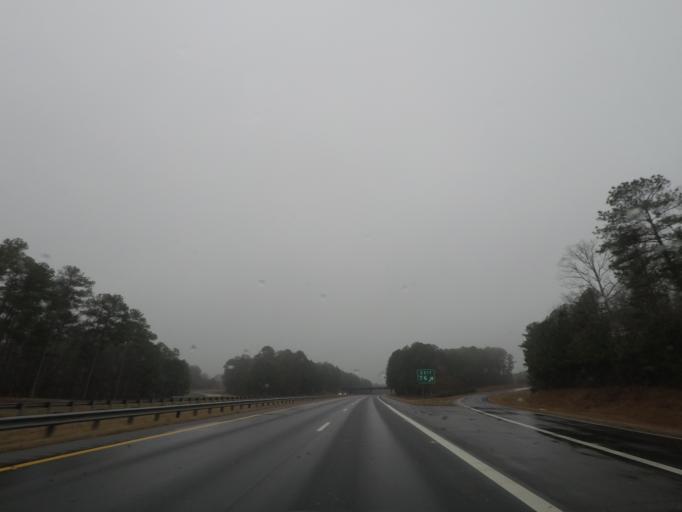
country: US
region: North Carolina
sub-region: Chatham County
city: Farmville
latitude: 35.5905
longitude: -79.1195
